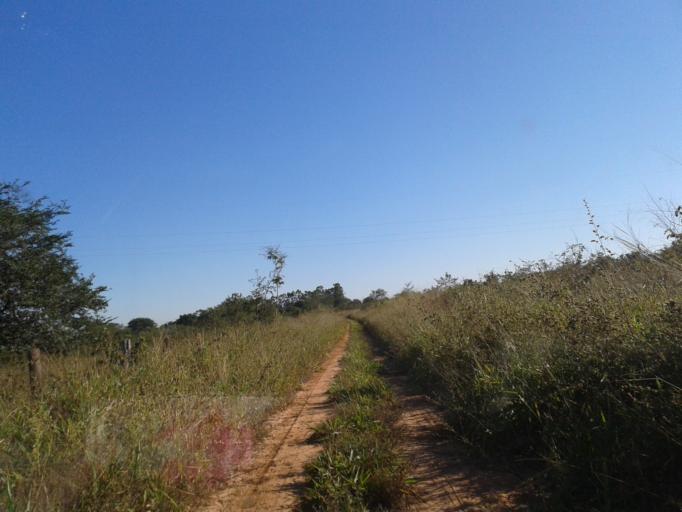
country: BR
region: Minas Gerais
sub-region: Santa Vitoria
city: Santa Vitoria
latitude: -19.0143
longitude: -50.3824
